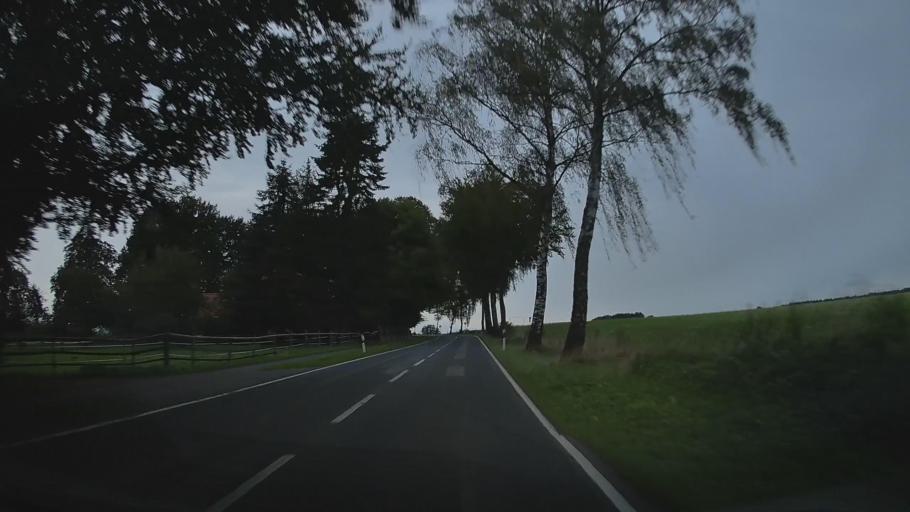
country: DE
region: Lower Saxony
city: Wildeshausen
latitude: 52.8992
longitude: 8.4822
